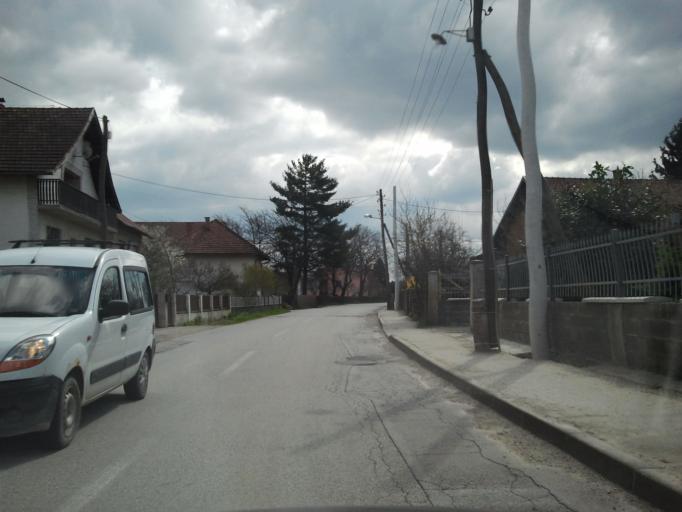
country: HR
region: Grad Zagreb
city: Zadvorsko
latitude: 45.7317
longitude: 15.9001
